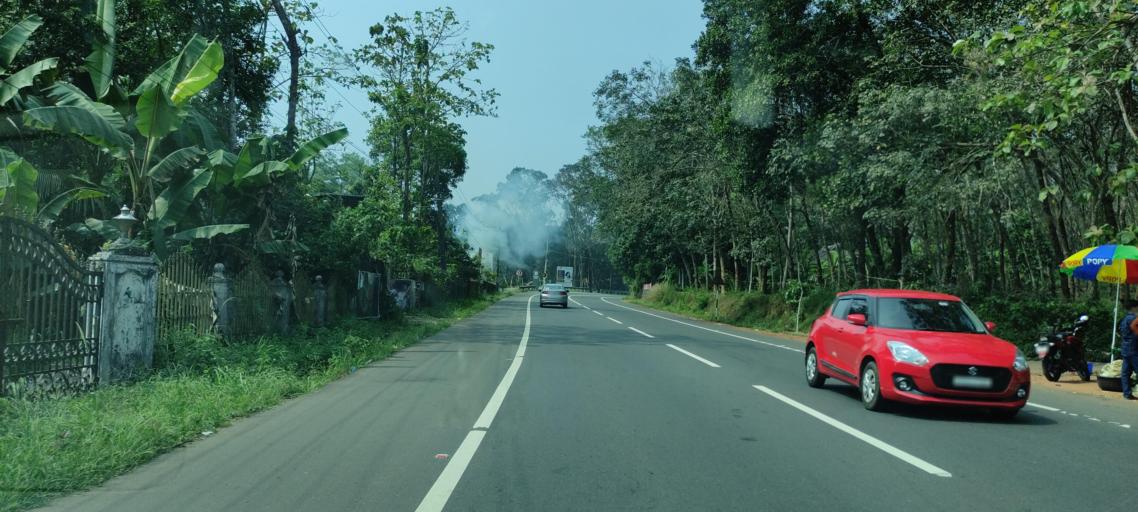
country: IN
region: Kerala
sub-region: Pattanamtitta
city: Adur
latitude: 9.1890
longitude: 76.7071
